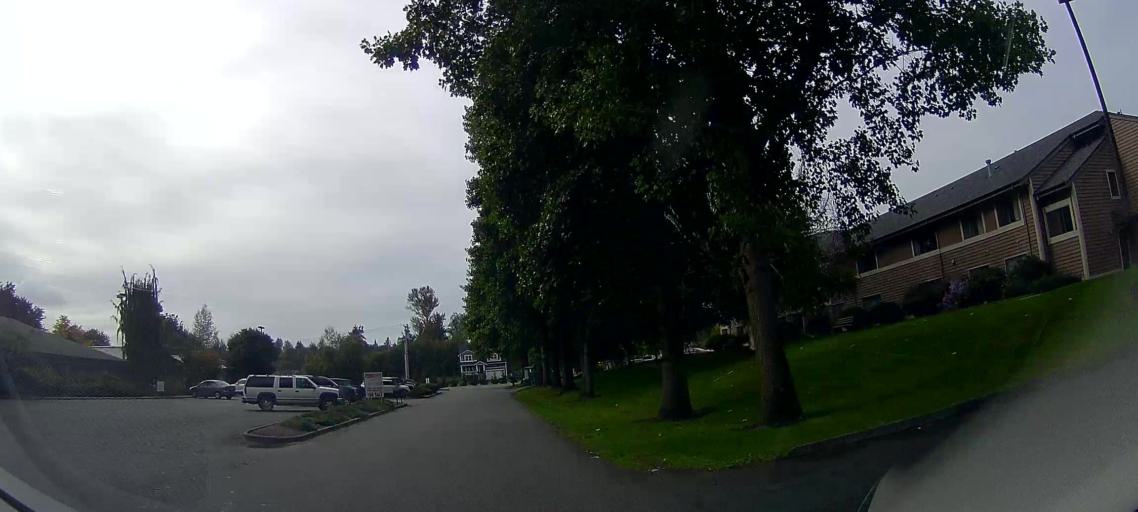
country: US
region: Washington
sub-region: Skagit County
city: Sedro-Woolley
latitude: 48.4955
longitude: -122.2788
